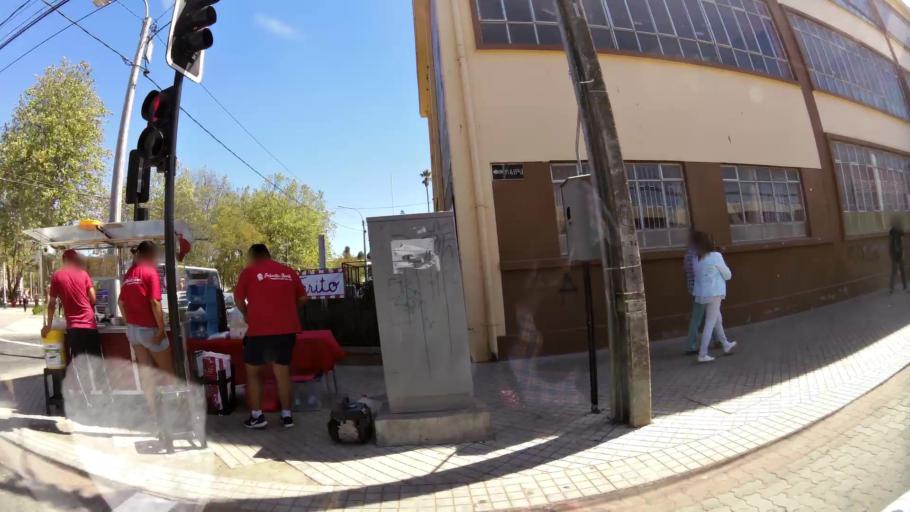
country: CL
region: Biobio
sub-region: Provincia de Concepcion
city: Penco
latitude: -36.7379
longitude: -72.9934
